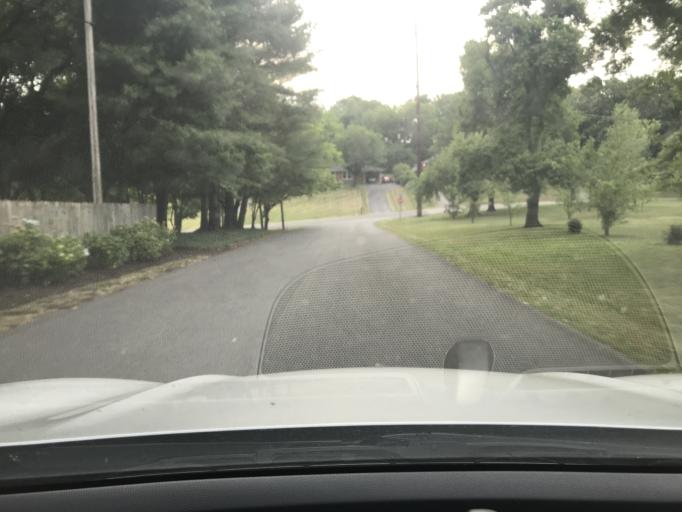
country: US
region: Tennessee
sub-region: Davidson County
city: Goodlettsville
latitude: 36.3069
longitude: -86.7132
